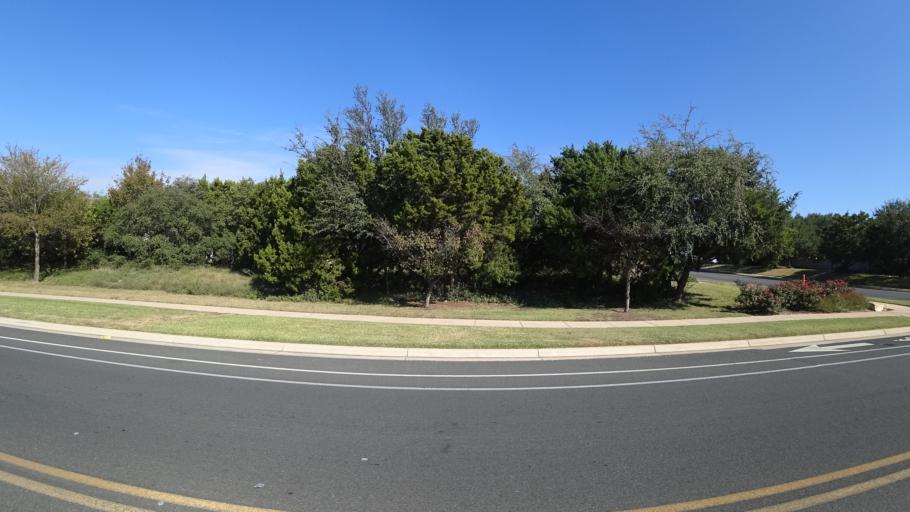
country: US
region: Texas
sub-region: Travis County
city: Hudson Bend
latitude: 30.3739
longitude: -97.8963
